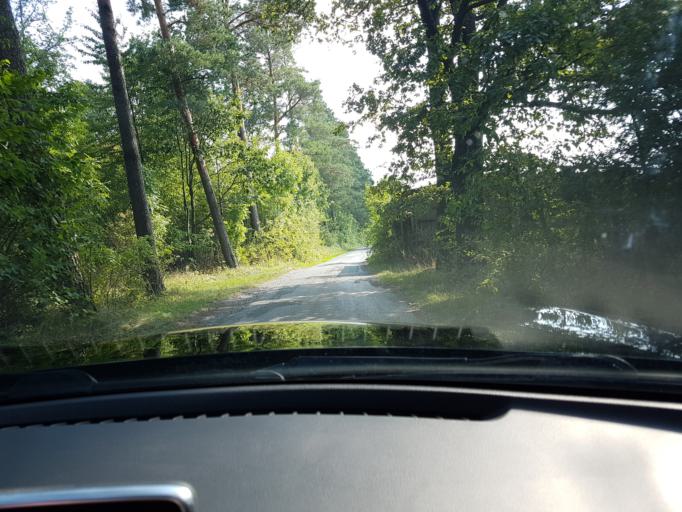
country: DE
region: Baden-Wuerttemberg
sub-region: Karlsruhe Region
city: Osterburken
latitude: 49.4264
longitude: 9.4535
